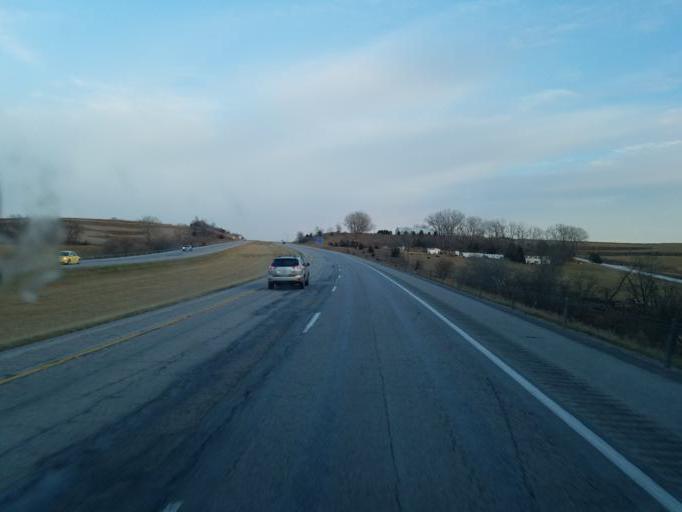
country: US
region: Iowa
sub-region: Harrison County
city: Missouri Valley
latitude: 41.4931
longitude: -95.8541
